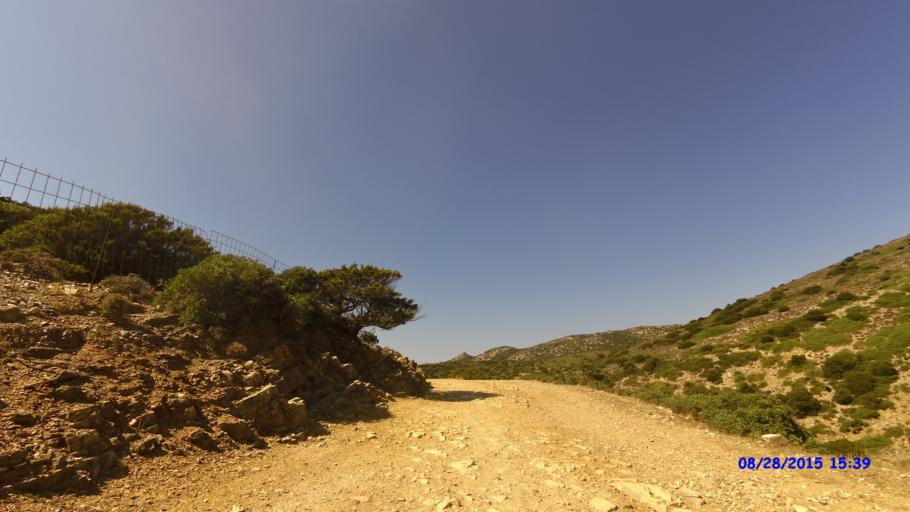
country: GR
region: South Aegean
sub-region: Nomos Kykladon
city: Antiparos
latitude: 36.9875
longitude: 25.0292
